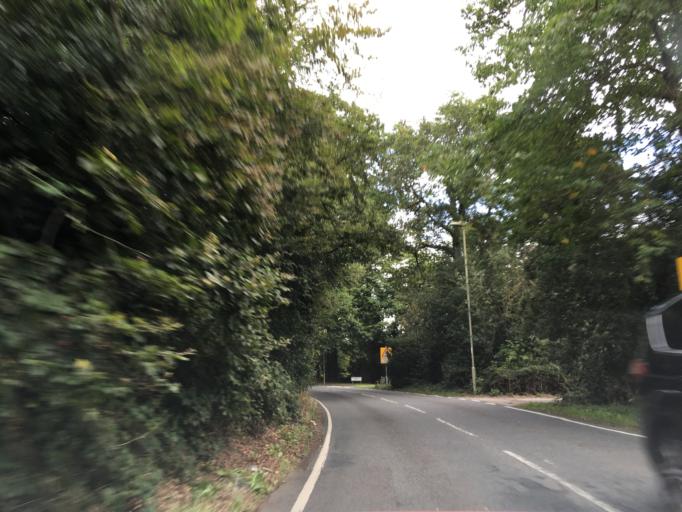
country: GB
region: England
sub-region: Hampshire
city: Chandlers Ford
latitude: 51.0005
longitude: -1.3677
